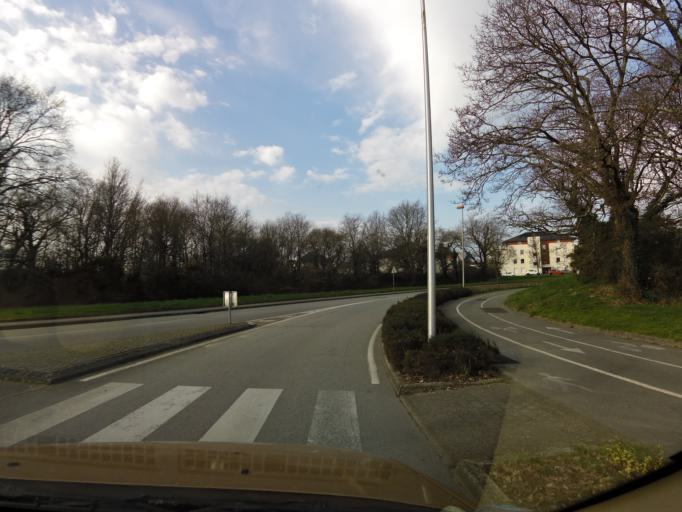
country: FR
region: Brittany
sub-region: Departement du Morbihan
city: Vannes
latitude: 47.6586
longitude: -2.7280
